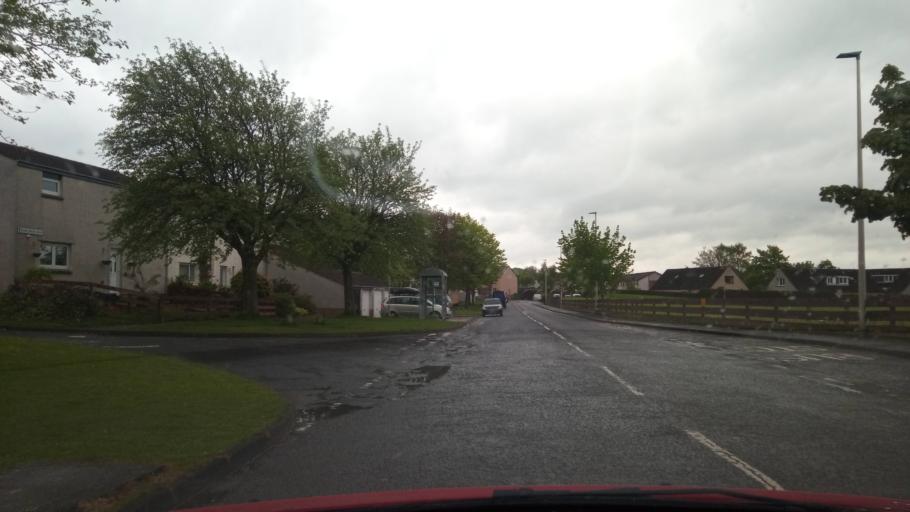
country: GB
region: Scotland
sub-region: The Scottish Borders
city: Jedburgh
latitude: 55.4742
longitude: -2.5458
